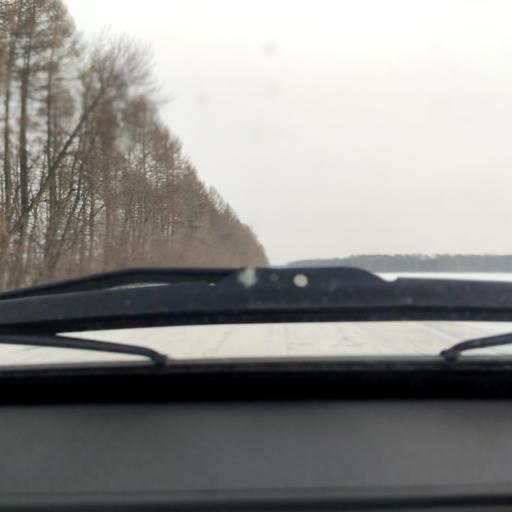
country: RU
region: Bashkortostan
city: Mikhaylovka
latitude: 54.8543
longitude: 55.8644
